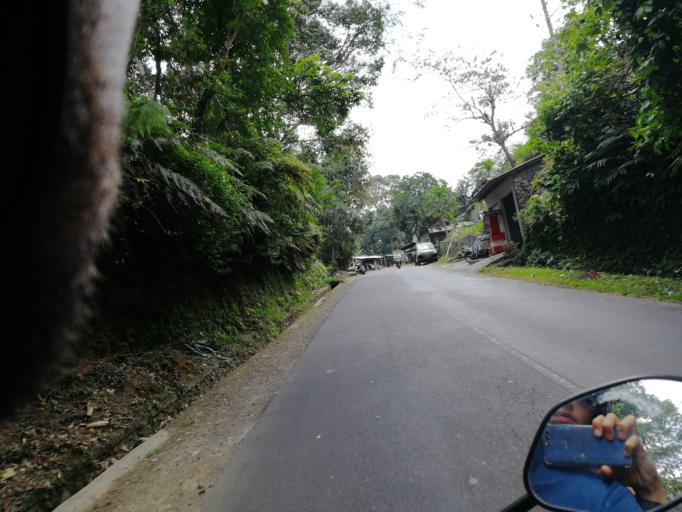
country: ID
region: Bali
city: Banjar Wates Tengah
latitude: -8.4536
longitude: 115.4525
